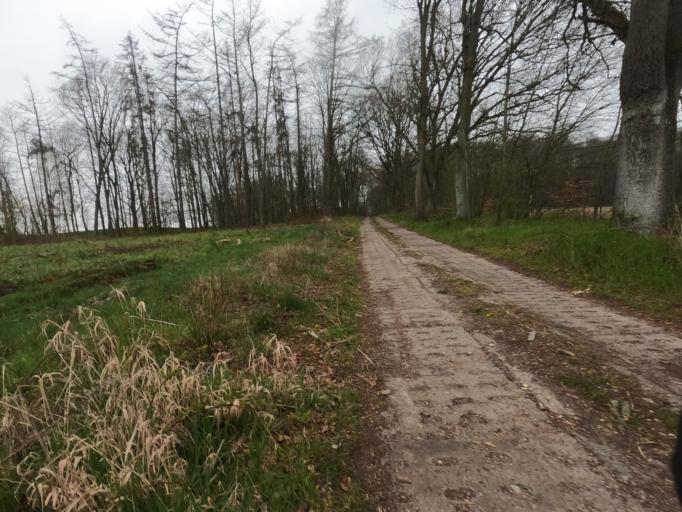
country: PL
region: West Pomeranian Voivodeship
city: Trzcinsko Zdroj
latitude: 52.9282
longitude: 14.6891
